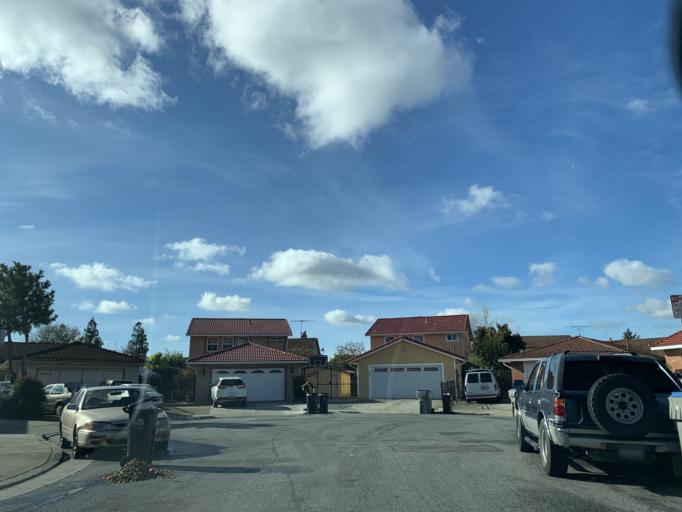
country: US
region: California
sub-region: Santa Clara County
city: Alum Rock
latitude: 37.3457
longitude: -121.8370
